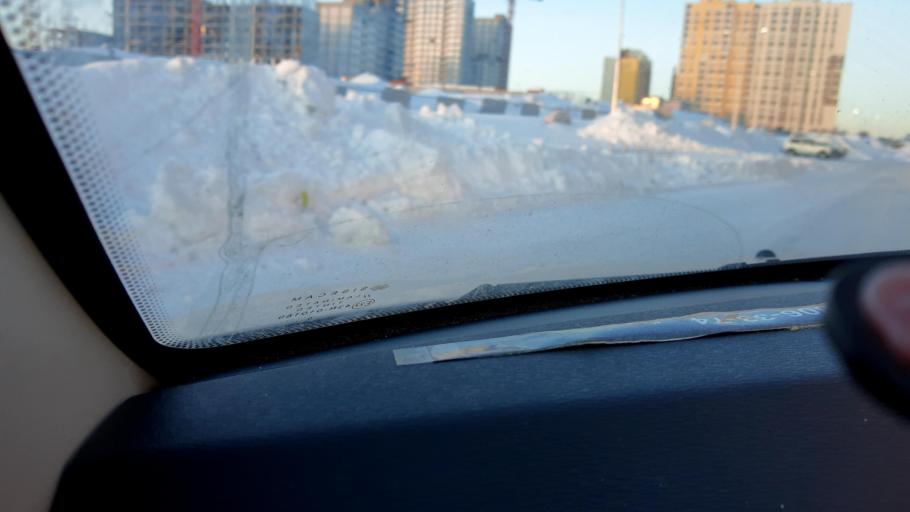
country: RU
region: Nizjnij Novgorod
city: Afonino
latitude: 56.2739
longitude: 44.0507
